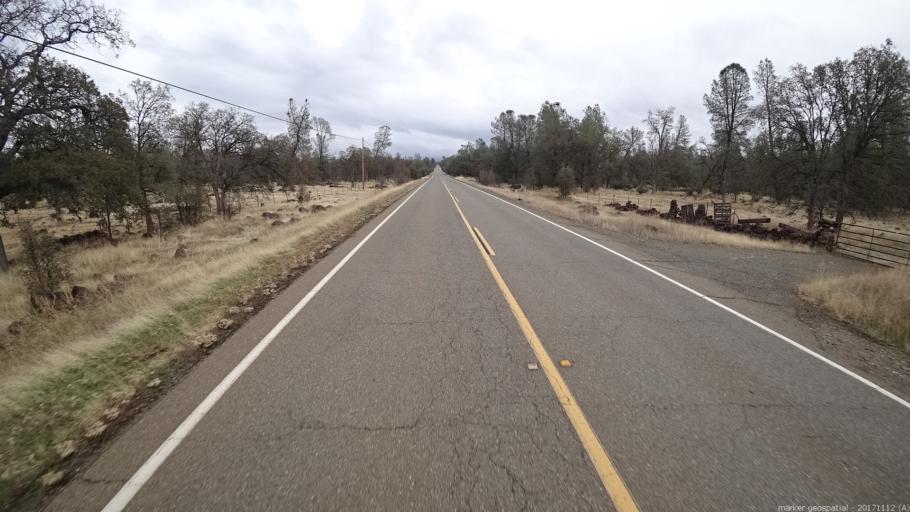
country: US
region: California
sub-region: Shasta County
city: Palo Cedro
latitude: 40.4812
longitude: -122.1025
